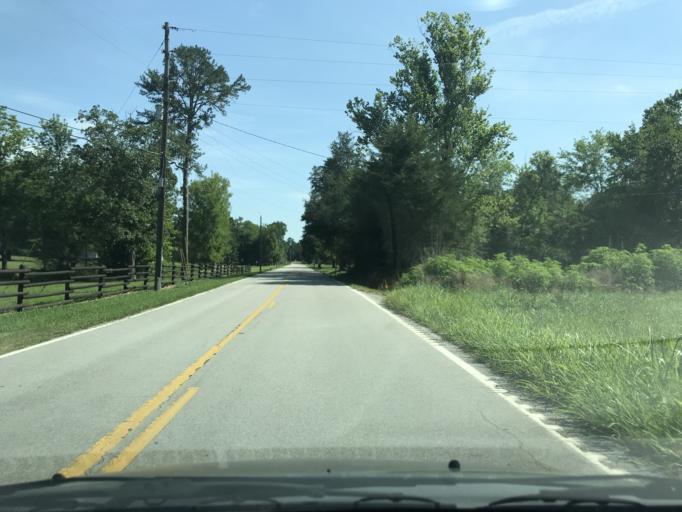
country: US
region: Tennessee
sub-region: Hamilton County
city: Sale Creek
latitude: 35.3345
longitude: -85.0071
